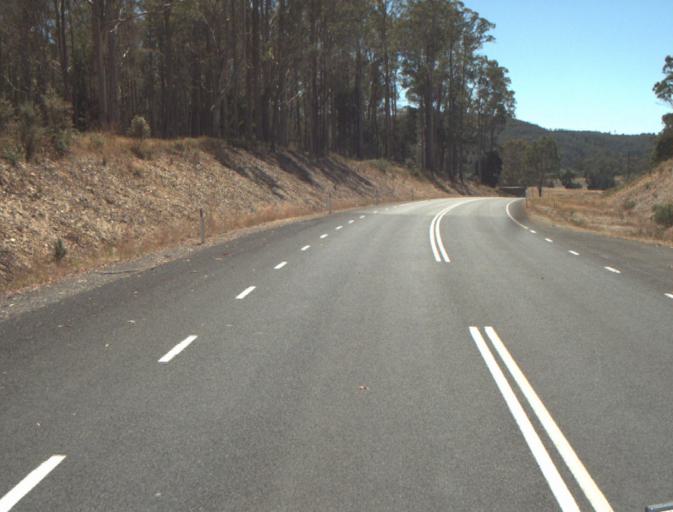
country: AU
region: Tasmania
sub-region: Launceston
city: Newstead
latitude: -41.3366
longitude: 147.3475
